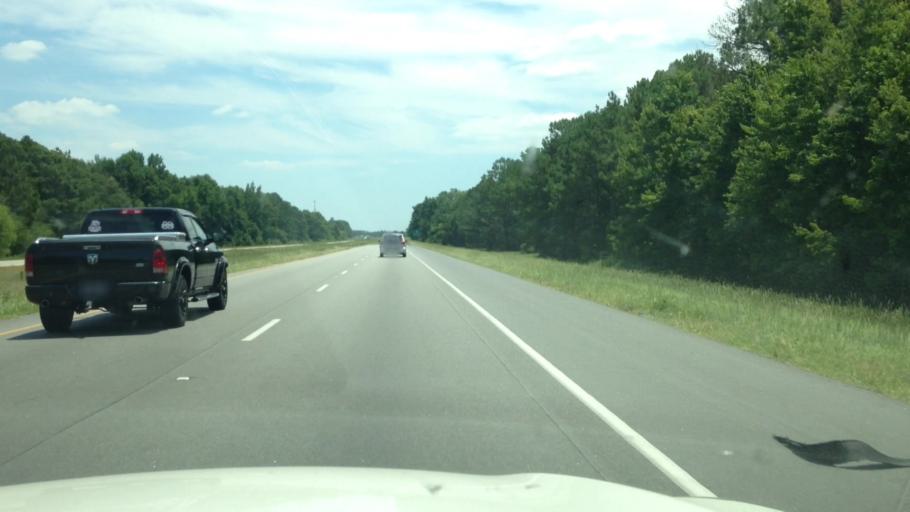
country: US
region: South Carolina
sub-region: Lee County
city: Bishopville
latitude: 34.1885
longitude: -80.2405
